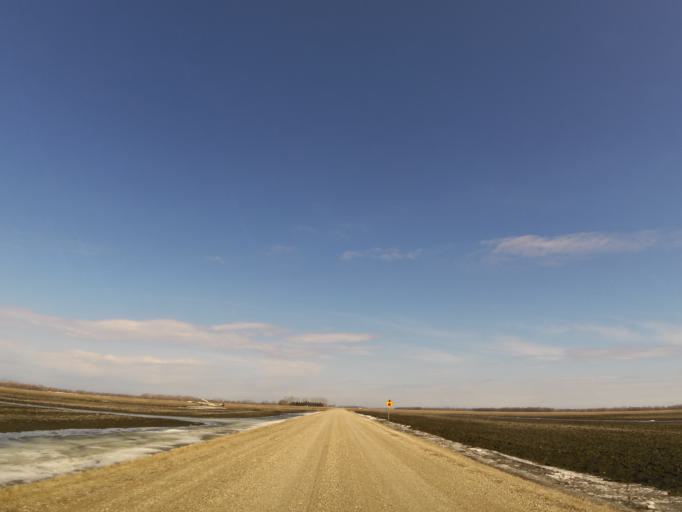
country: US
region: North Dakota
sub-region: Walsh County
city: Grafton
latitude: 48.4086
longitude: -97.1686
